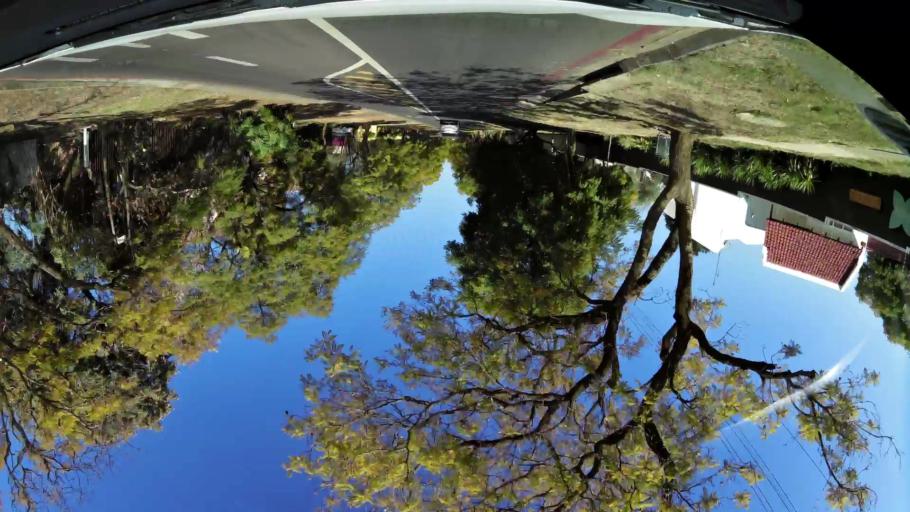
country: ZA
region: Gauteng
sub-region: City of Tshwane Metropolitan Municipality
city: Pretoria
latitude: -25.7675
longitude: 28.2496
